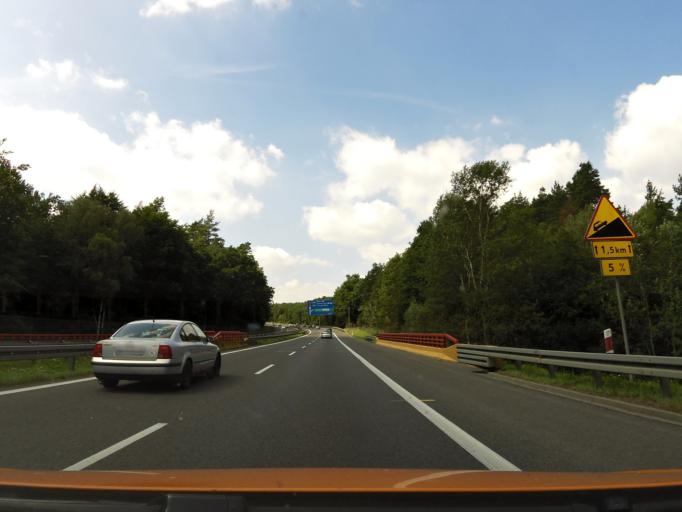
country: PL
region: West Pomeranian Voivodeship
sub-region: Szczecin
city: Szczecin
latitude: 53.3660
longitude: 14.6349
